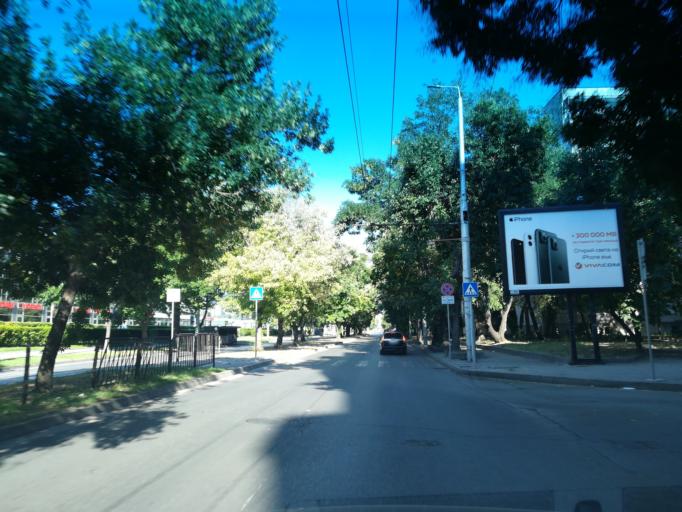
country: BG
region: Plovdiv
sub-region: Obshtina Plovdiv
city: Plovdiv
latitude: 42.1619
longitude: 24.7340
